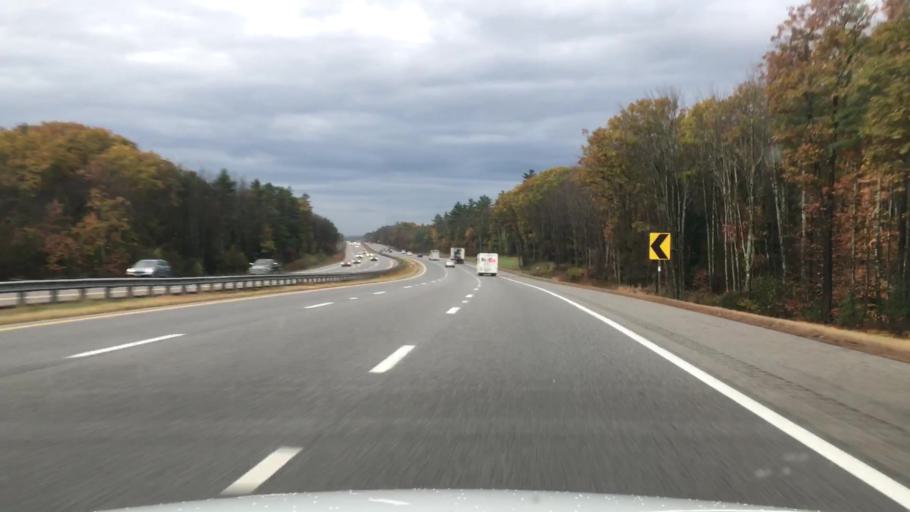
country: US
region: Maine
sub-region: York County
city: Biddeford
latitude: 43.4625
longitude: -70.5233
